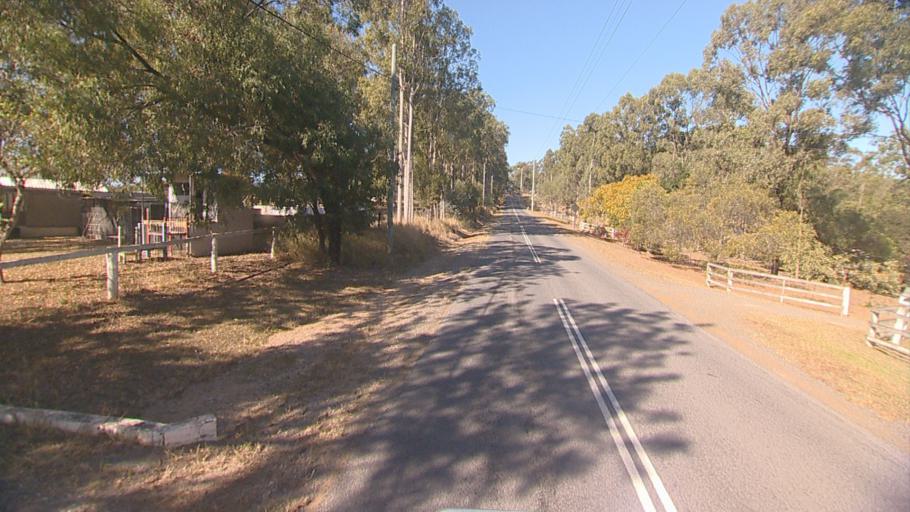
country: AU
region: Queensland
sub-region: Logan
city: Cedar Vale
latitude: -27.8828
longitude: 153.0163
